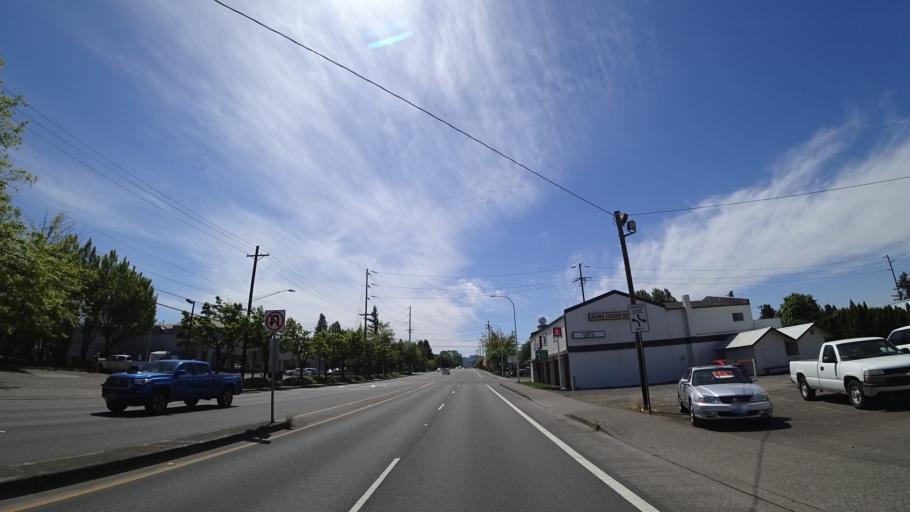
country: US
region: Oregon
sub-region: Washington County
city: Aloha
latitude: 45.4931
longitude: -122.8673
